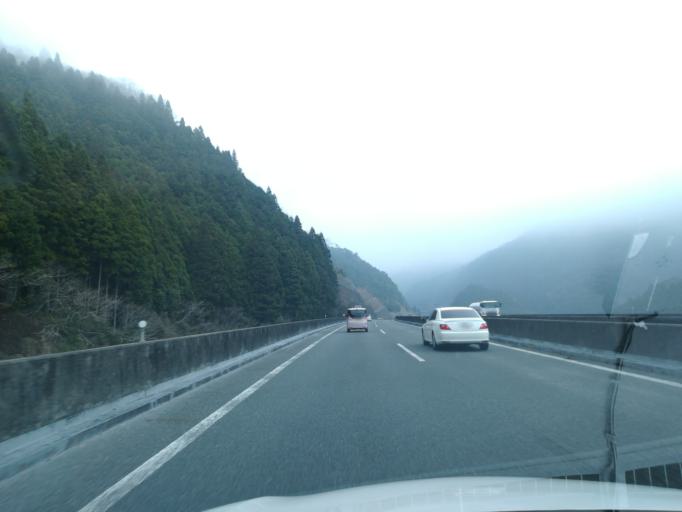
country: JP
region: Ehime
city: Kawanoecho
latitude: 33.7830
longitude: 133.6618
